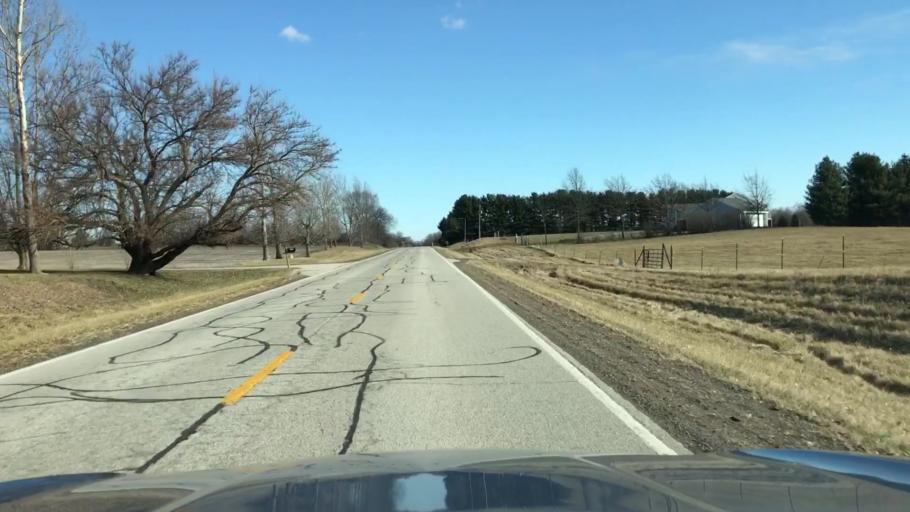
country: US
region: Illinois
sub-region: McLean County
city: Lexington
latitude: 40.6482
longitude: -88.8547
